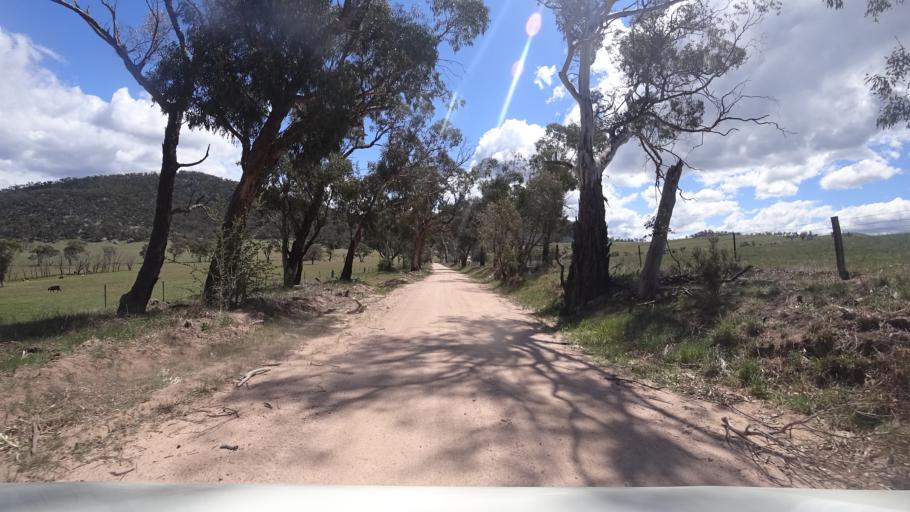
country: AU
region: New South Wales
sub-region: Oberon
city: Oberon
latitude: -33.5613
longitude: 149.9362
